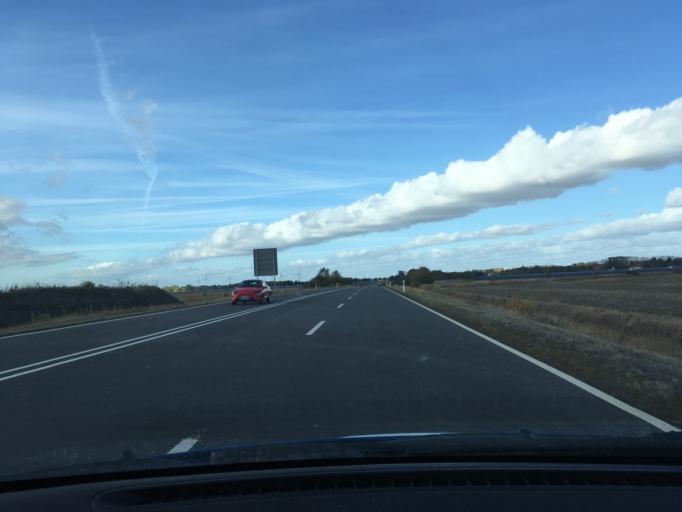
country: DE
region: Brandenburg
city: Perleberg
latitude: 53.0655
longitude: 11.8311
